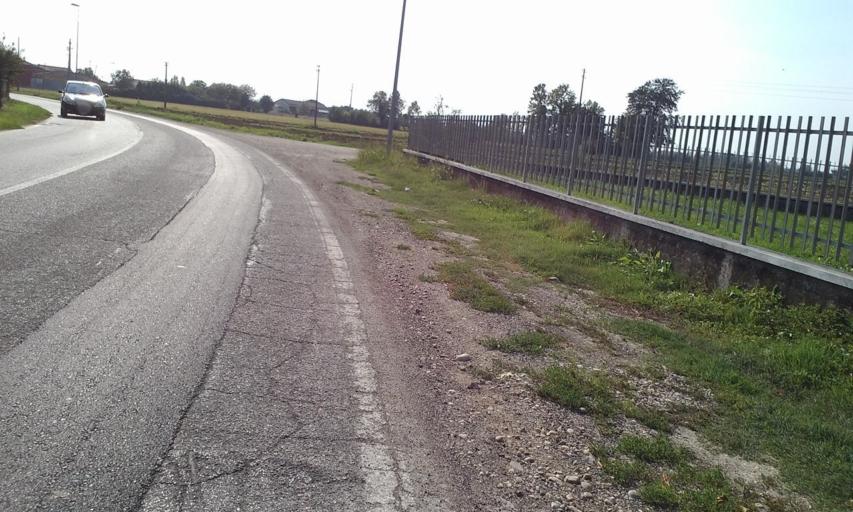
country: IT
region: Veneto
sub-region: Provincia di Verona
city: Povegliano Veronese
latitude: 45.3558
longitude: 10.8845
